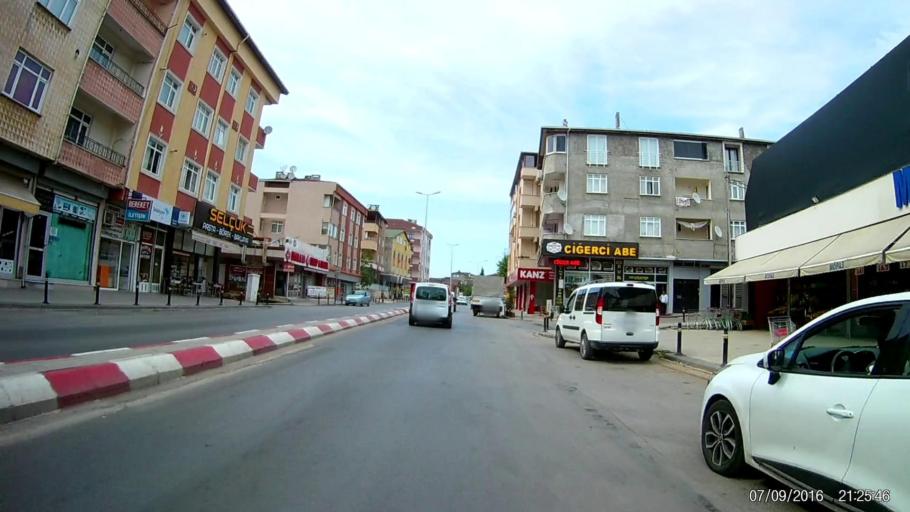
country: TR
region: Istanbul
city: Sultanbeyli
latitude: 40.9794
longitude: 29.2658
